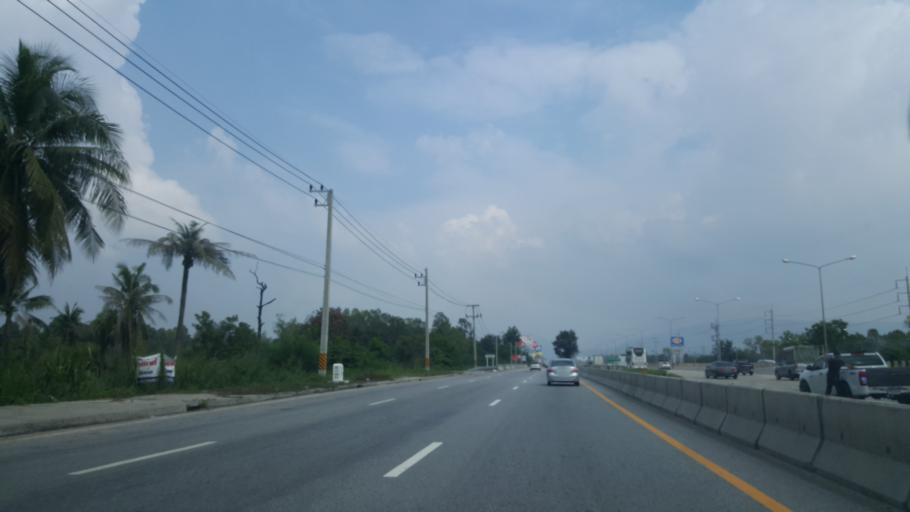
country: TH
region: Chon Buri
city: Si Racha
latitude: 13.1849
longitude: 100.9965
